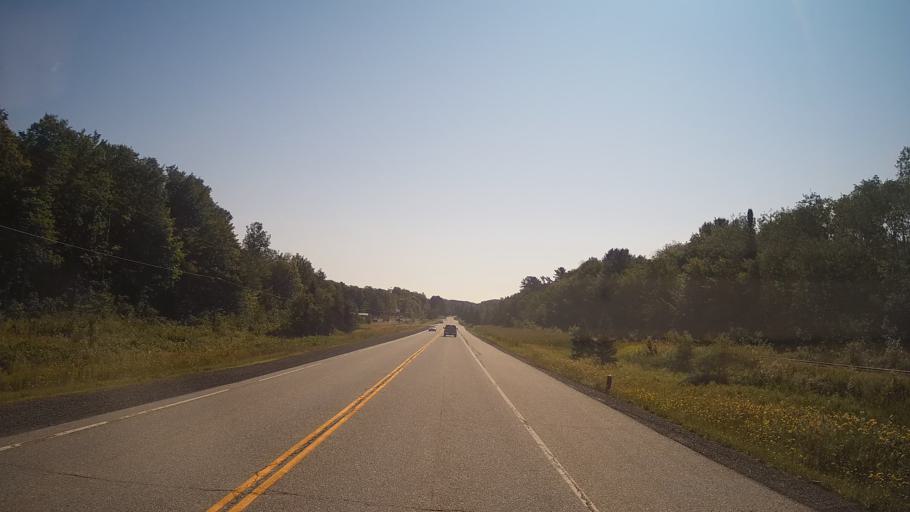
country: CA
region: Ontario
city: Elliot Lake
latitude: 46.2051
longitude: -82.4269
